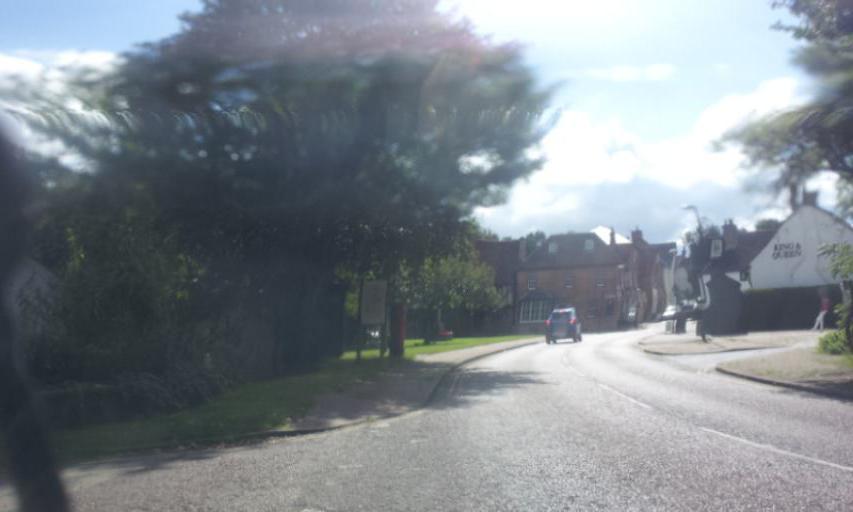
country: GB
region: England
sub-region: Kent
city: Larkfield
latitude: 51.2883
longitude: 0.4393
